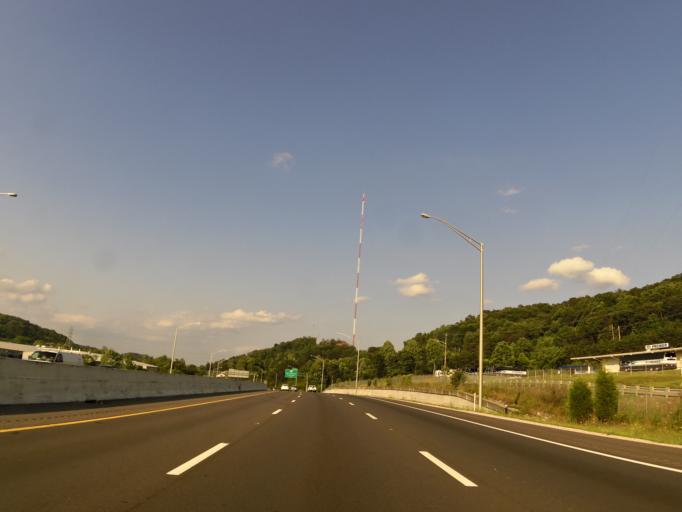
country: US
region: Tennessee
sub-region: Knox County
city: Knoxville
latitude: 36.0078
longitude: -83.9424
